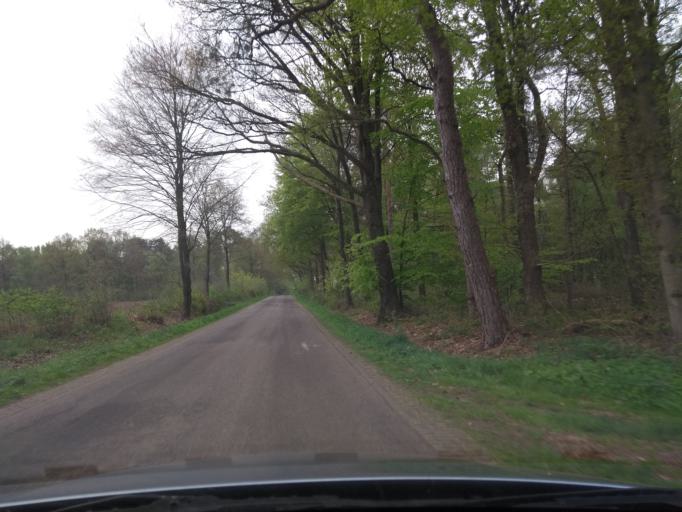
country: DE
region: Lower Saxony
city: Getelo
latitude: 52.4293
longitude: 6.9058
